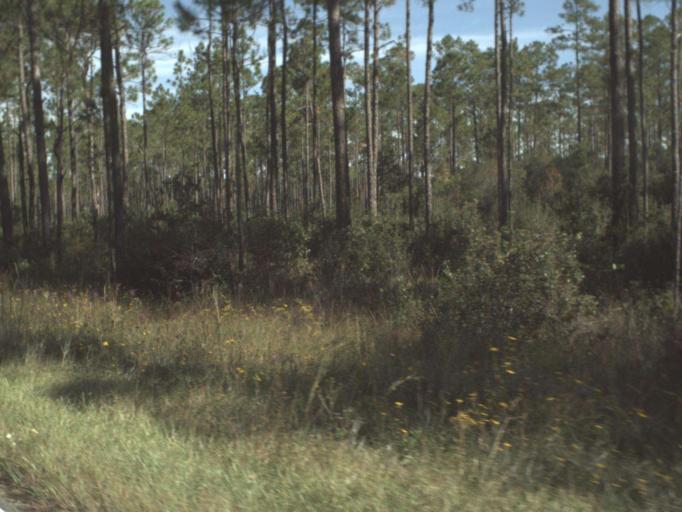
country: US
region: Florida
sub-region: Gulf County
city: Wewahitchka
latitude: 30.1014
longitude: -84.9857
